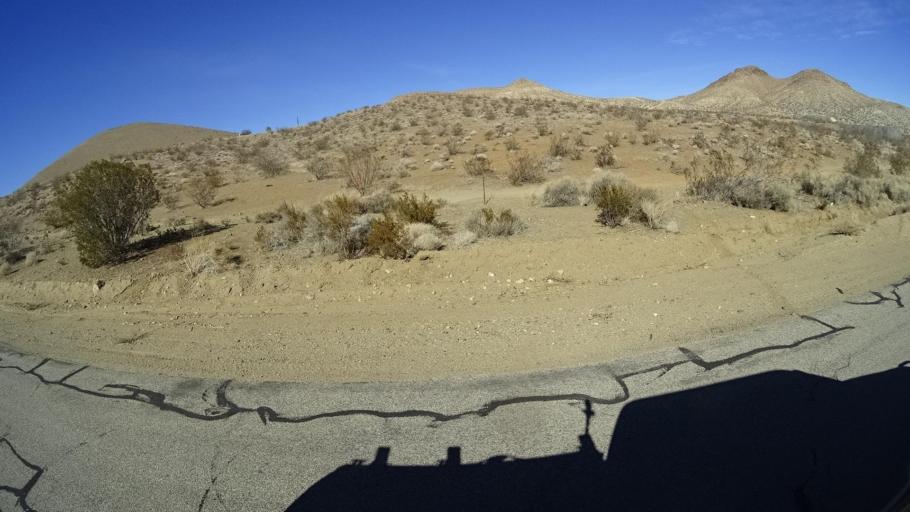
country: US
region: California
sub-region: Kern County
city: Ridgecrest
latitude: 35.3519
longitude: -117.6317
